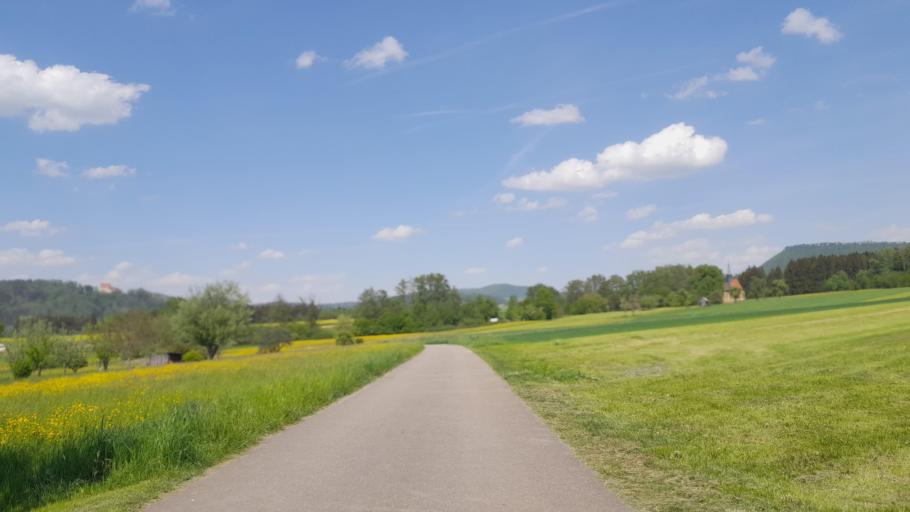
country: DE
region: Baden-Wuerttemberg
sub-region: Regierungsbezirk Stuttgart
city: Gingen an der Fils
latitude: 48.6740
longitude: 9.7800
